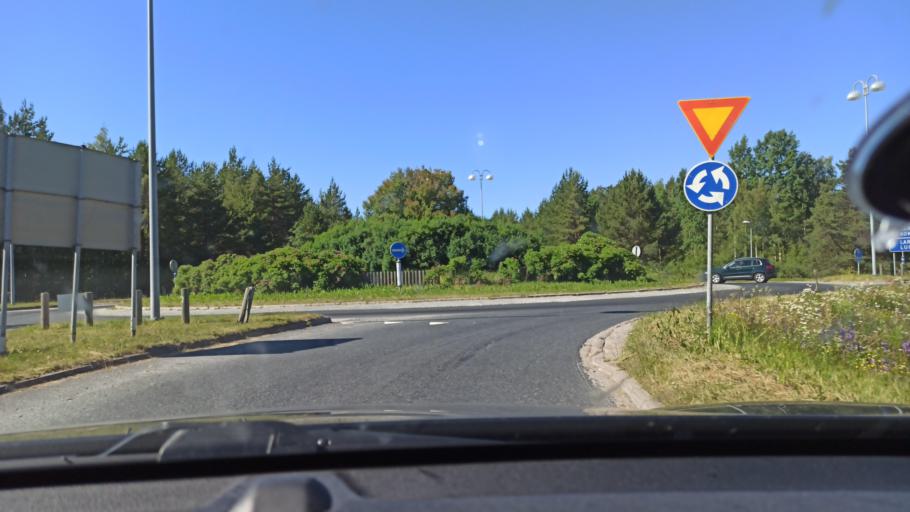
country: FI
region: Ostrobothnia
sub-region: Jakobstadsregionen
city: Jakobstad
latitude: 63.6540
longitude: 22.7148
